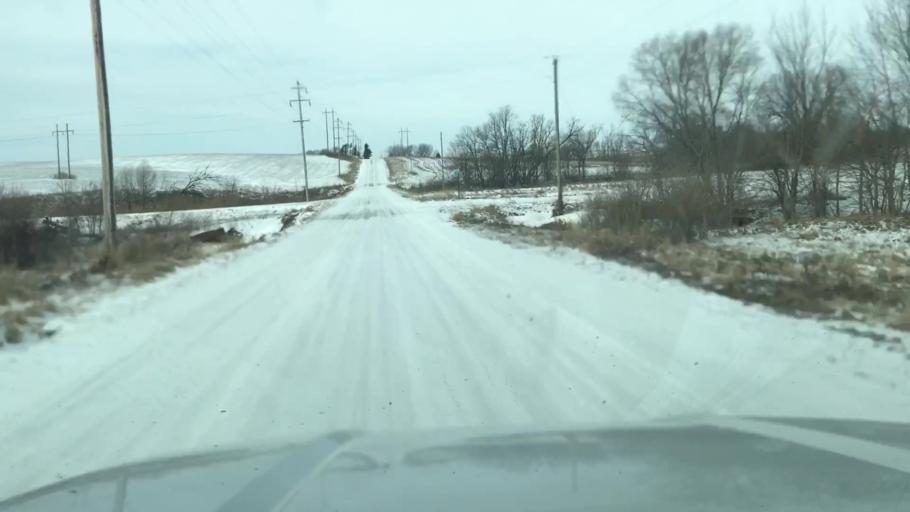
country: US
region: Missouri
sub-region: Holt County
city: Mound City
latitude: 40.1301
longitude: -95.0784
